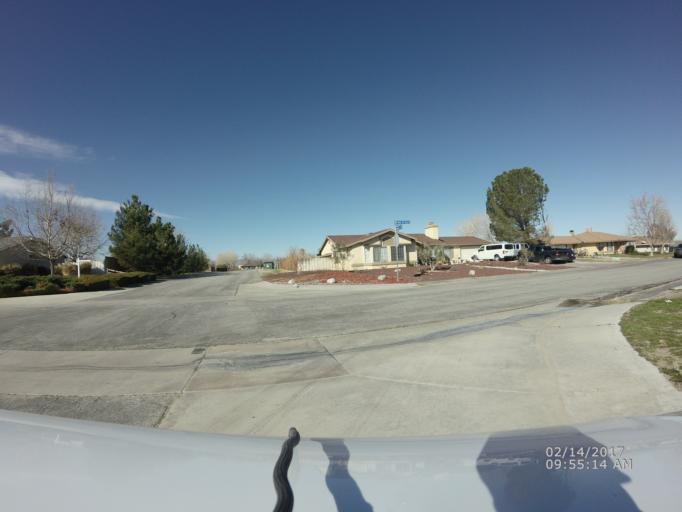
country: US
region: California
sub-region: Los Angeles County
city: Littlerock
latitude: 34.5538
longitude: -117.9613
